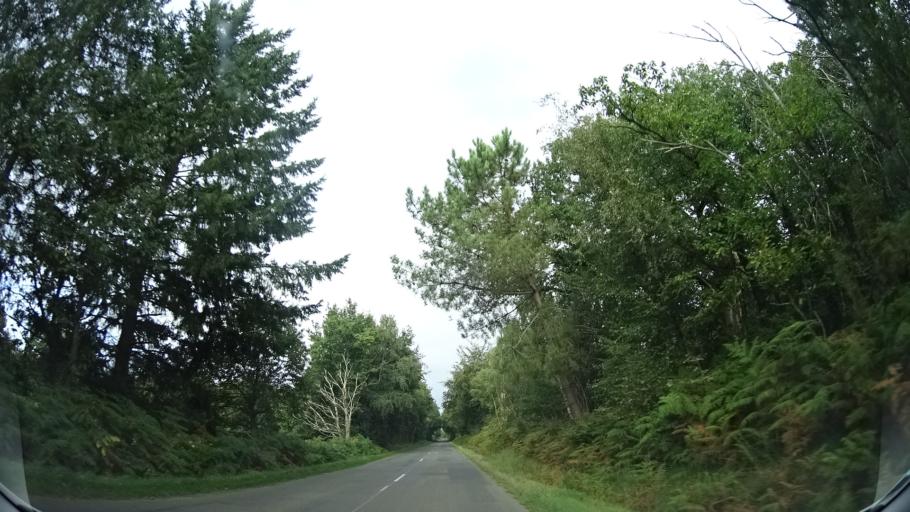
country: FR
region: Brittany
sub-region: Departement d'Ille-et-Vilaine
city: Guipel
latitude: 48.2994
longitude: -1.7487
